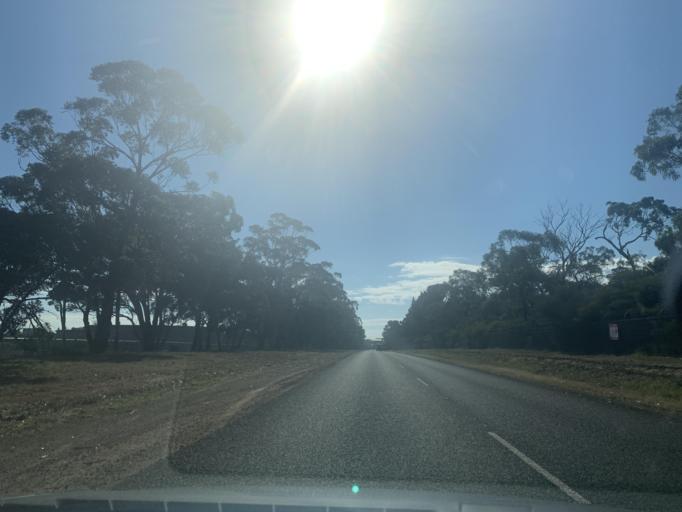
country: AU
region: Victoria
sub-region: Mornington Peninsula
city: Hastings
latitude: -38.2946
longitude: 145.2105
